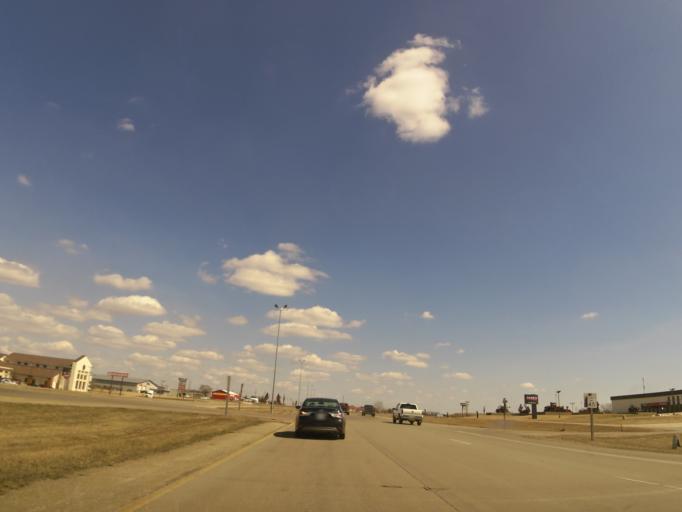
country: US
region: South Dakota
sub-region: Codington County
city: Watertown
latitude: 44.8900
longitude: -97.0546
